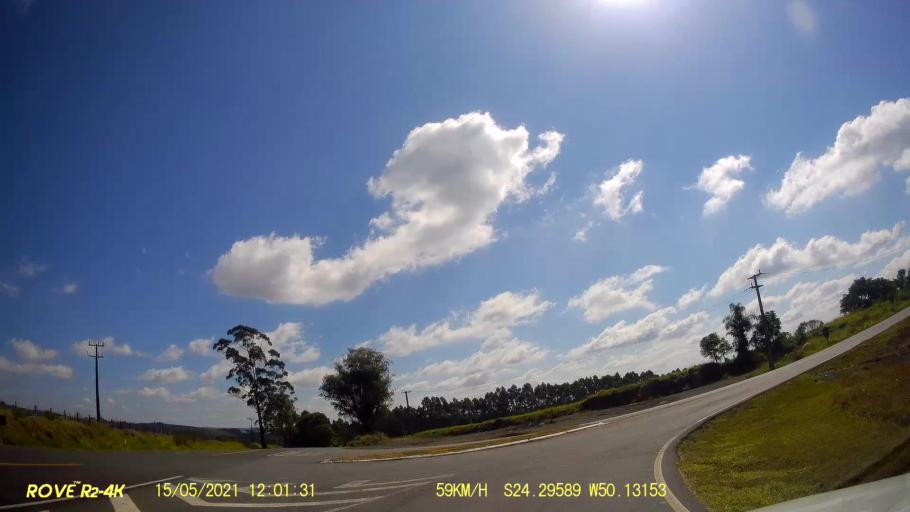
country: BR
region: Parana
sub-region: Pirai Do Sul
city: Pirai do Sul
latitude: -24.2960
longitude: -50.1309
